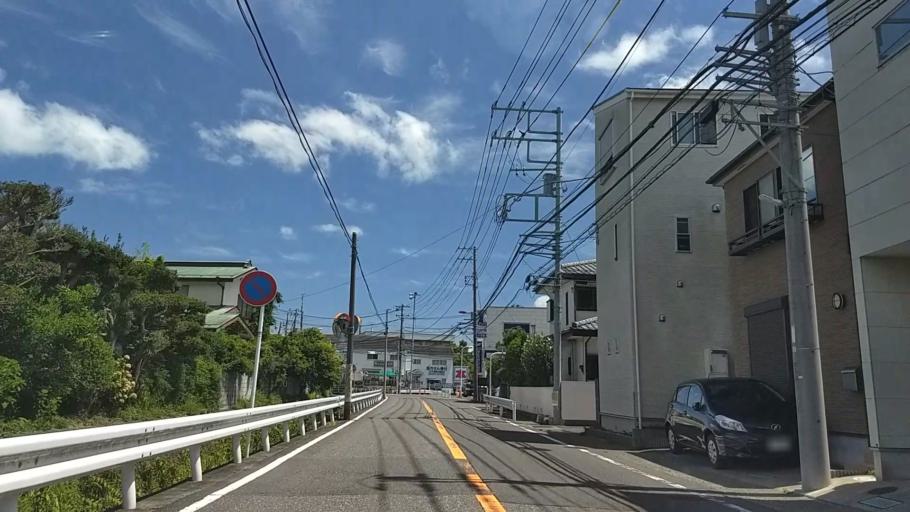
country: JP
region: Kanagawa
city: Kamakura
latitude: 35.3425
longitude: 139.5360
